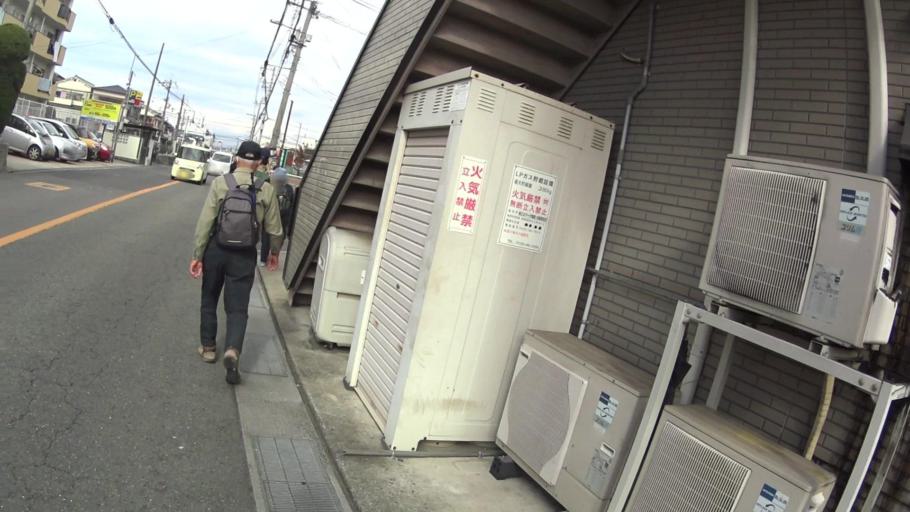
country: JP
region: Osaka
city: Kashihara
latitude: 34.5606
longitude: 135.5922
